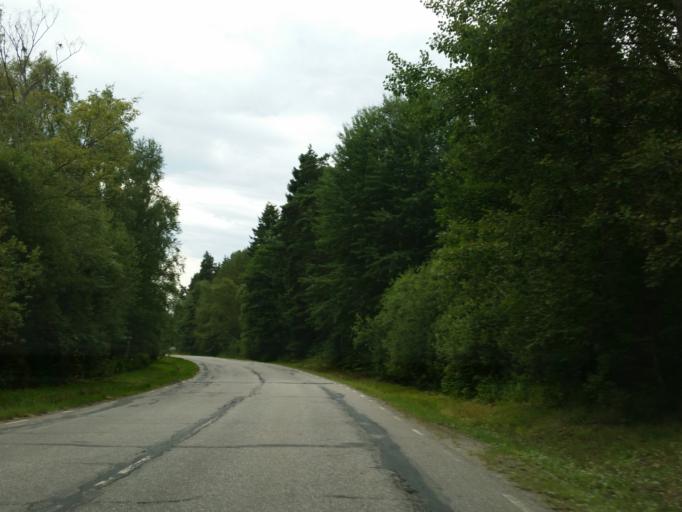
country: SE
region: Stockholm
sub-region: Sodertalje Kommun
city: Soedertaelje
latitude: 59.2115
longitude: 17.6529
